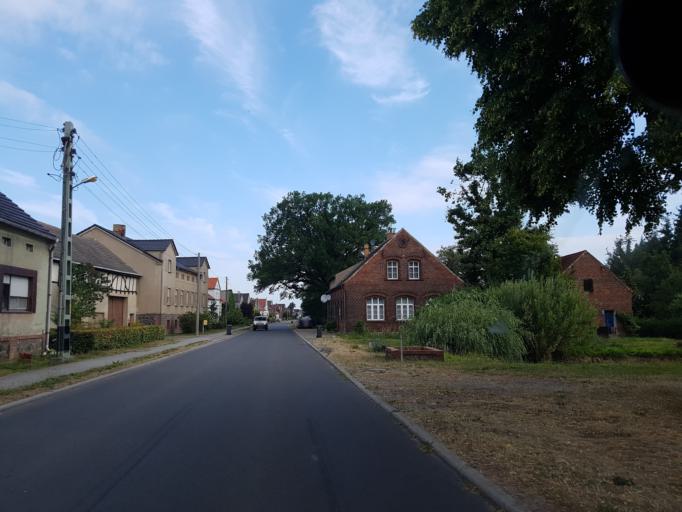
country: DE
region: Brandenburg
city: Luckau
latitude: 51.8363
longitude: 13.6412
